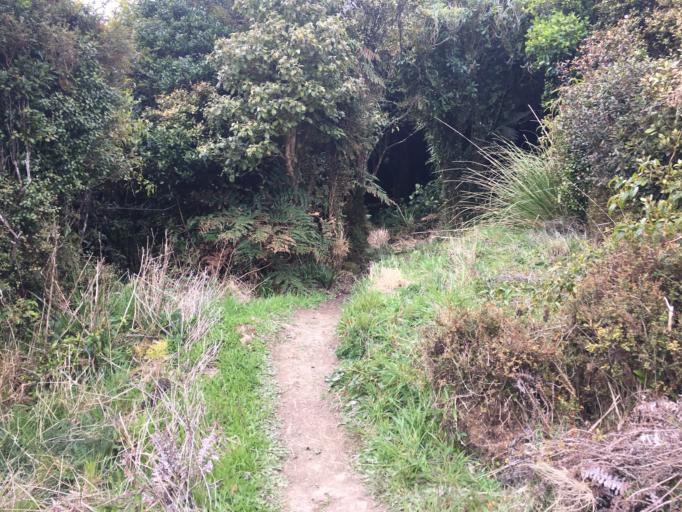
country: NZ
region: Manawatu-Wanganui
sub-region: Palmerston North City
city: Palmerston North
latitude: -40.4849
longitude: 175.6331
